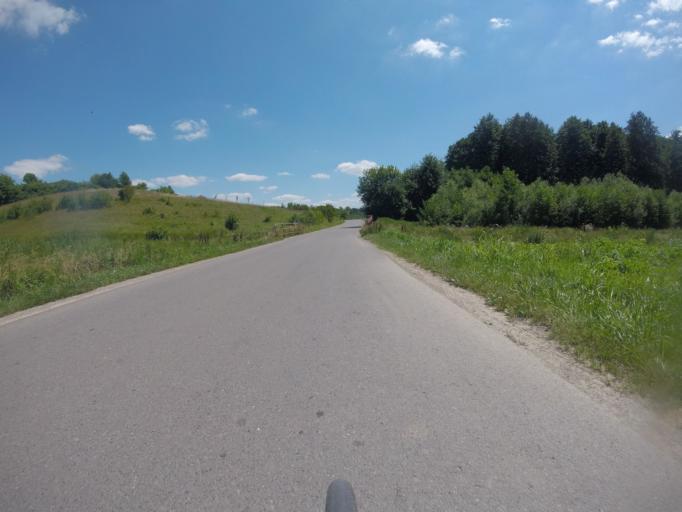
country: HR
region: Karlovacka
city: Ozalj
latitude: 45.6619
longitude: 15.4957
